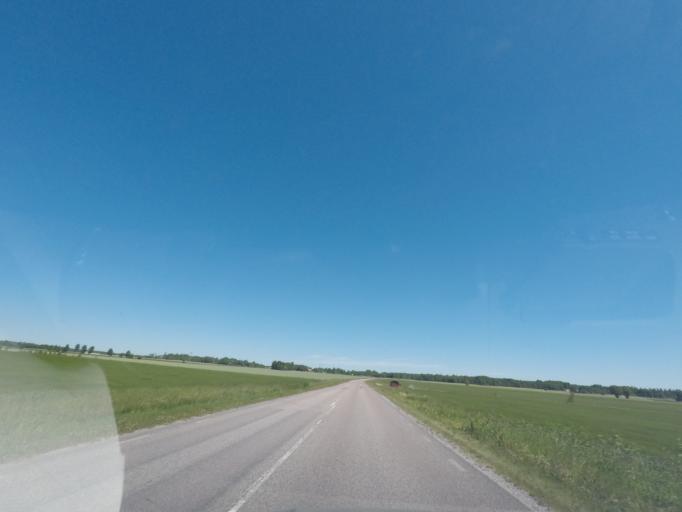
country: SE
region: Vaestmanland
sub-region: Vasteras
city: Tillberga
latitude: 59.6481
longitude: 16.6835
